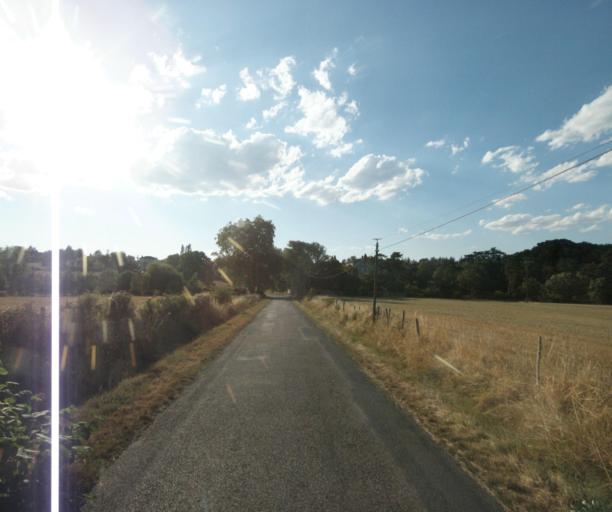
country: FR
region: Rhone-Alpes
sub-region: Departement du Rhone
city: Lentilly
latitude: 45.8293
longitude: 4.6744
